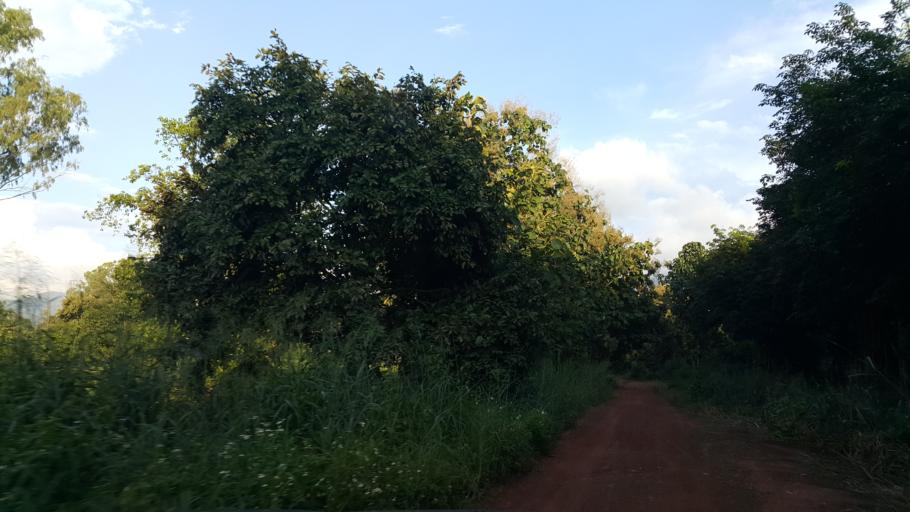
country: TH
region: Chiang Mai
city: Mae On
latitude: 18.7443
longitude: 99.2436
